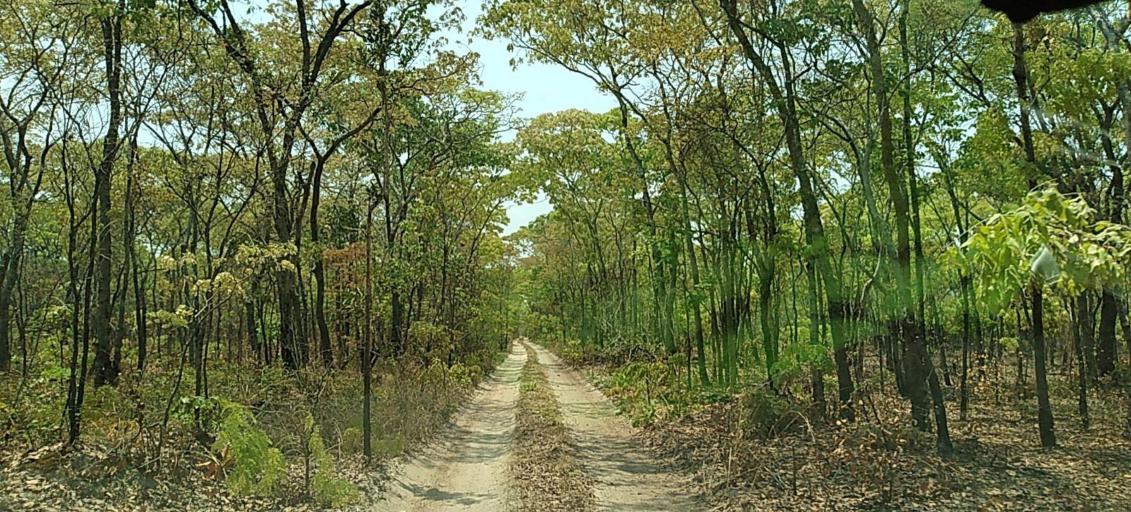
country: ZM
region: North-Western
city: Kabompo
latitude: -13.6521
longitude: 24.4713
